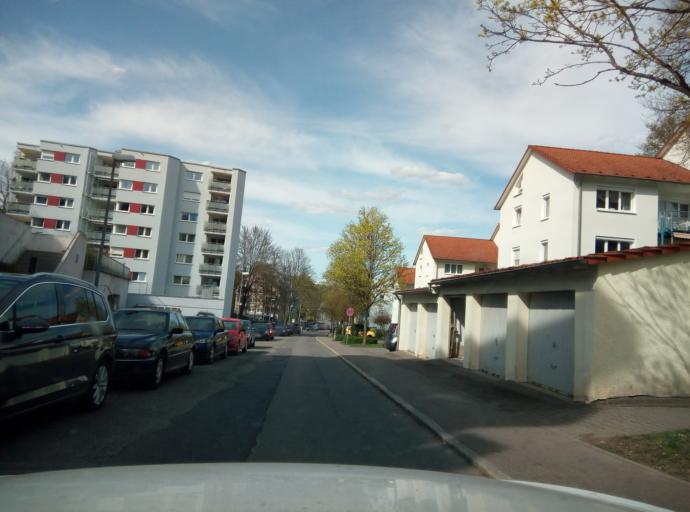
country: DE
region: Baden-Wuerttemberg
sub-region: Tuebingen Region
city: Tuebingen
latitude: 48.5072
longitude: 9.0743
